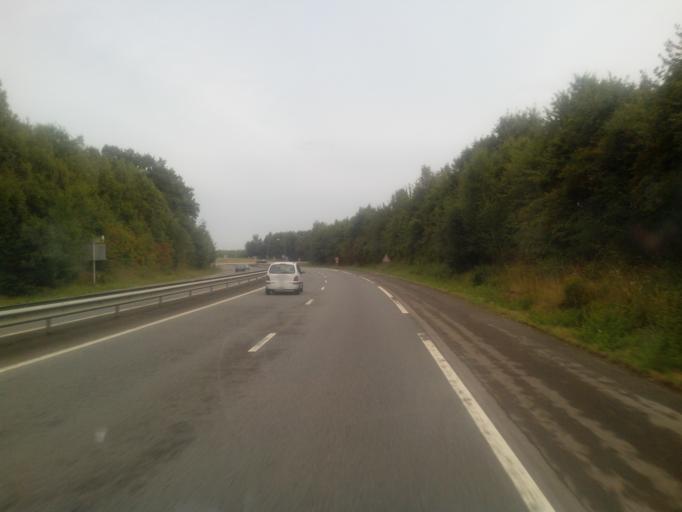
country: FR
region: Brittany
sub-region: Departement d'Ille-et-Vilaine
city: Cesson-Sevigne
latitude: 48.1384
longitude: -1.6267
